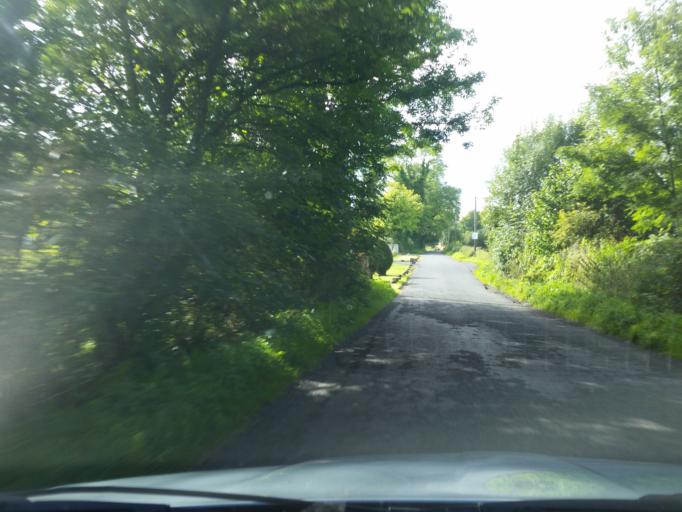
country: IE
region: Ulster
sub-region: County Monaghan
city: Clones
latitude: 54.1913
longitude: -7.2439
